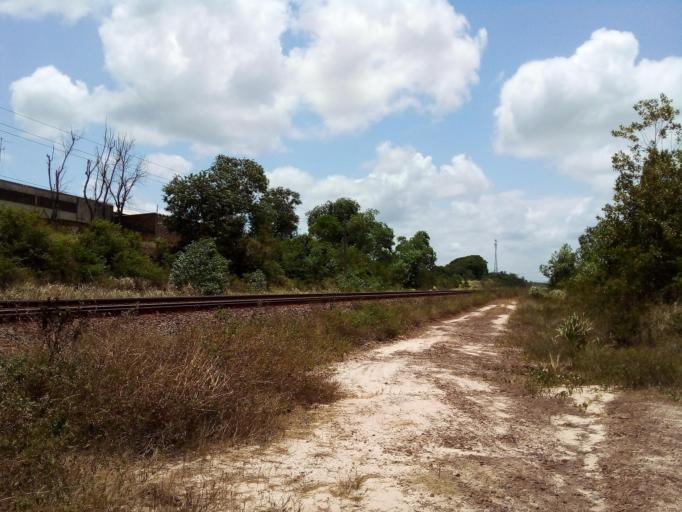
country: BR
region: Maranhao
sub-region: Sao Luis
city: Sao Luis
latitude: -2.7024
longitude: -44.3121
